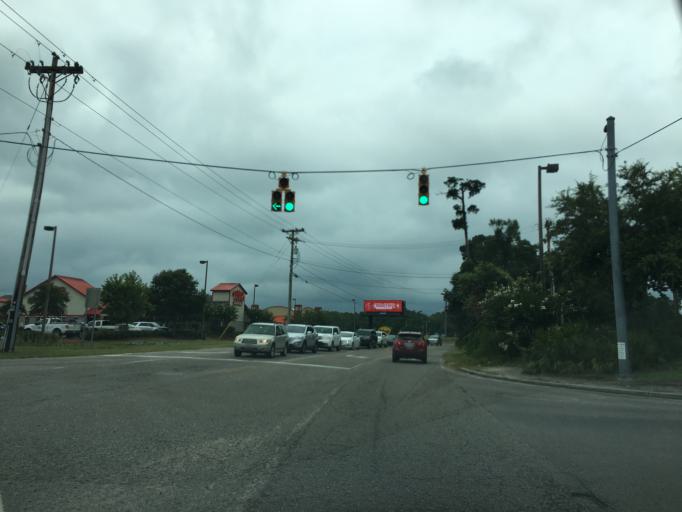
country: US
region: South Carolina
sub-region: Horry County
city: North Myrtle Beach
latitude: 33.7848
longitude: -78.7705
